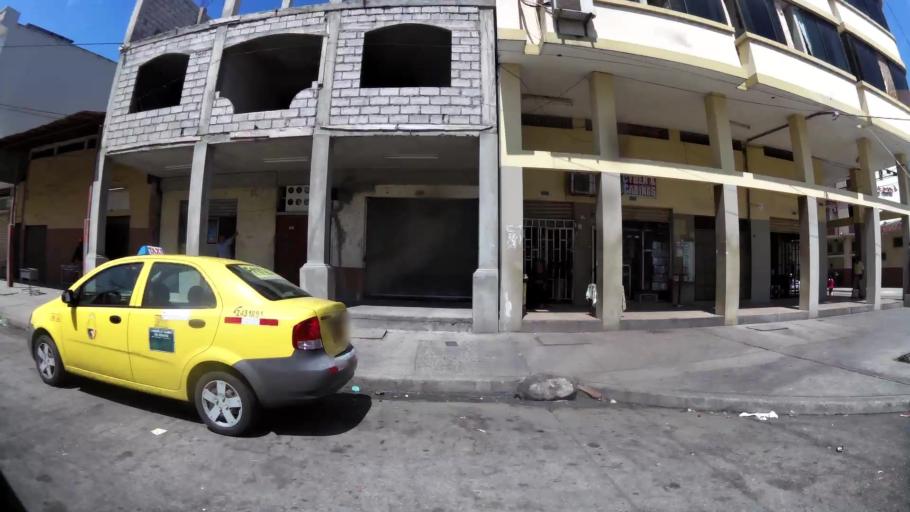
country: EC
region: Guayas
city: Guayaquil
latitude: -2.1955
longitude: -79.8932
